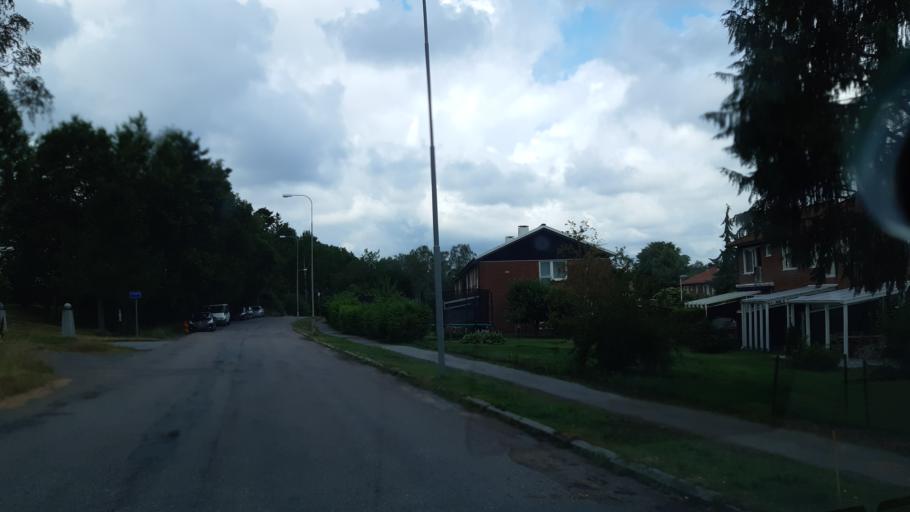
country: SE
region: Vaestra Goetaland
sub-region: Partille Kommun
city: Partille
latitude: 57.7153
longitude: 12.0598
